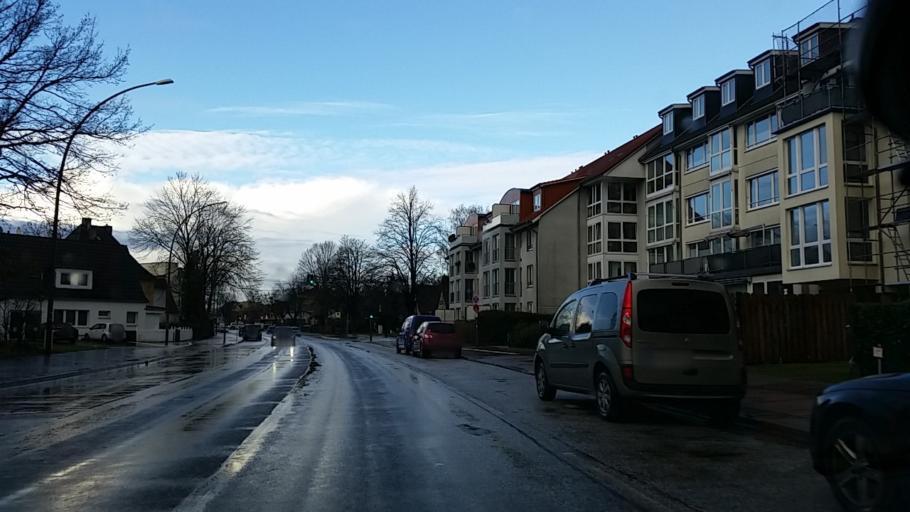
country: DE
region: Schleswig-Holstein
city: Halstenbek
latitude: 53.5968
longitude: 9.8661
